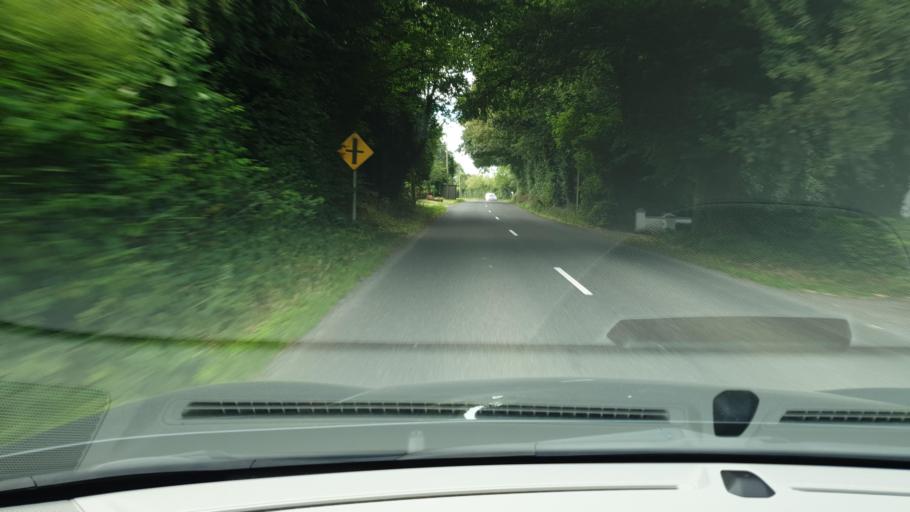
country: IE
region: Leinster
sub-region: An Mhi
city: Dunshaughlin
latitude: 53.5577
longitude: -6.6019
